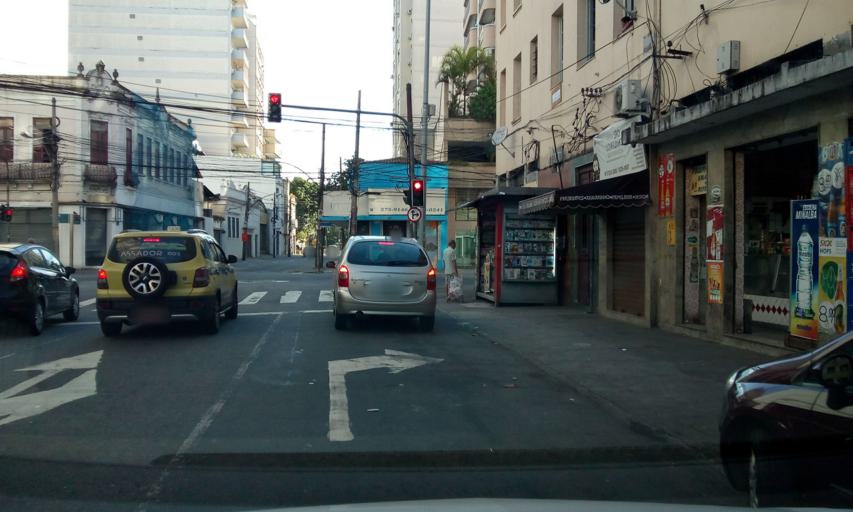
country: BR
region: Rio de Janeiro
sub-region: Rio De Janeiro
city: Rio de Janeiro
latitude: -22.9545
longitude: -43.1815
